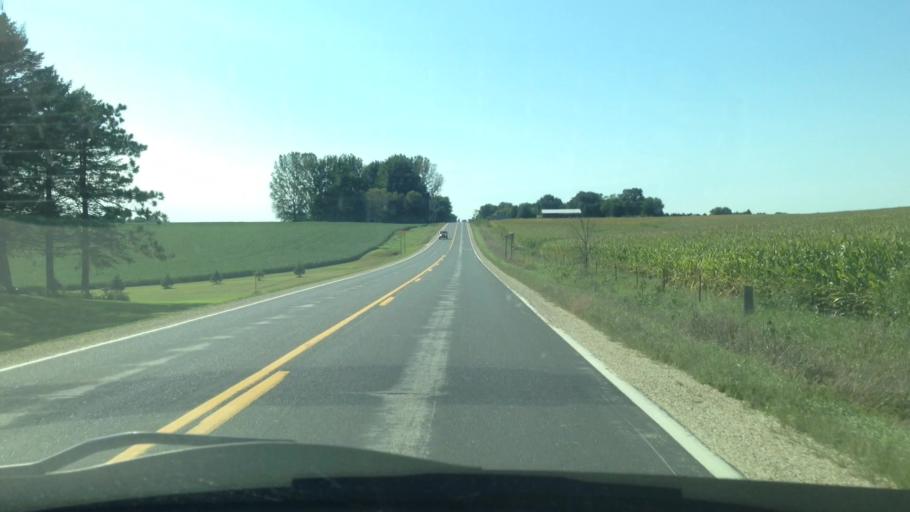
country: US
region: Minnesota
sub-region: Winona County
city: Lewiston
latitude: 43.9404
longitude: -91.7823
